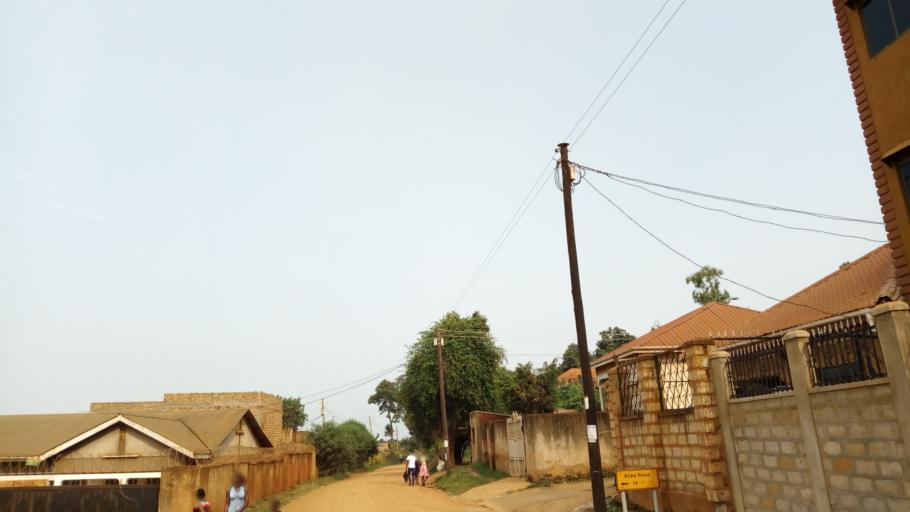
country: UG
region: Central Region
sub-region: Wakiso District
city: Kireka
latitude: 0.3168
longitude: 32.6482
